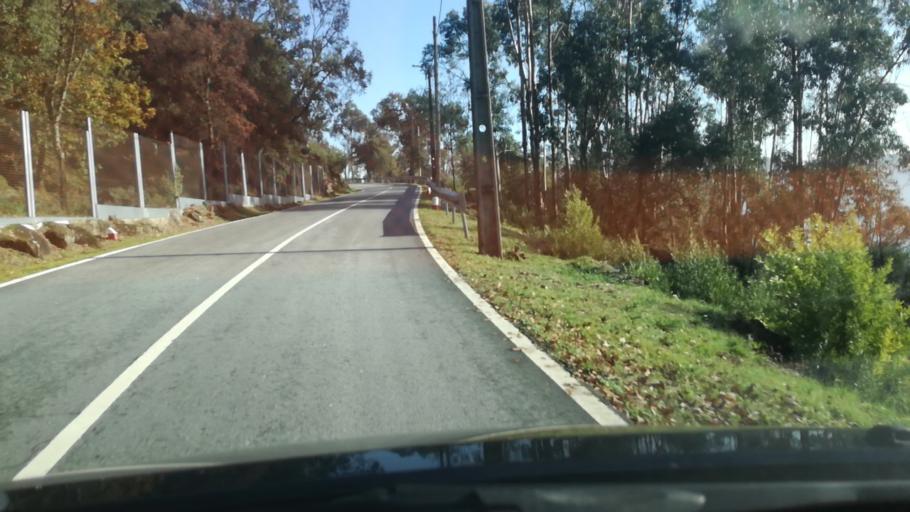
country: PT
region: Braga
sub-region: Guimaraes
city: Ponte
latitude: 41.5260
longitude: -8.3164
